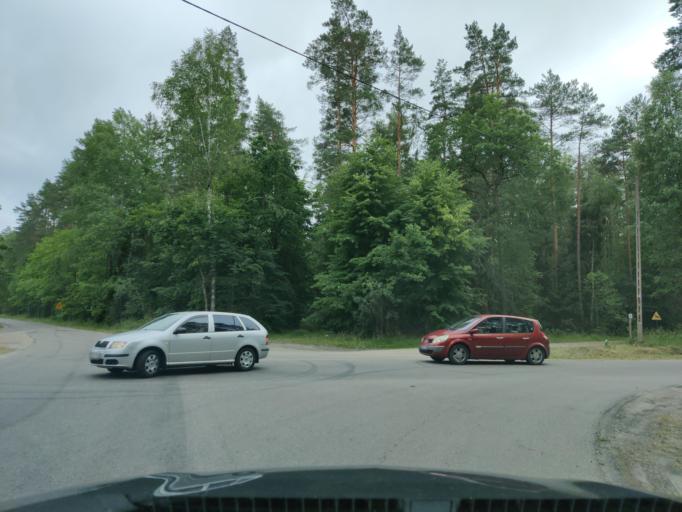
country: PL
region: Warmian-Masurian Voivodeship
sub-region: Powiat piski
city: Ruciane-Nida
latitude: 53.5535
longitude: 21.4759
